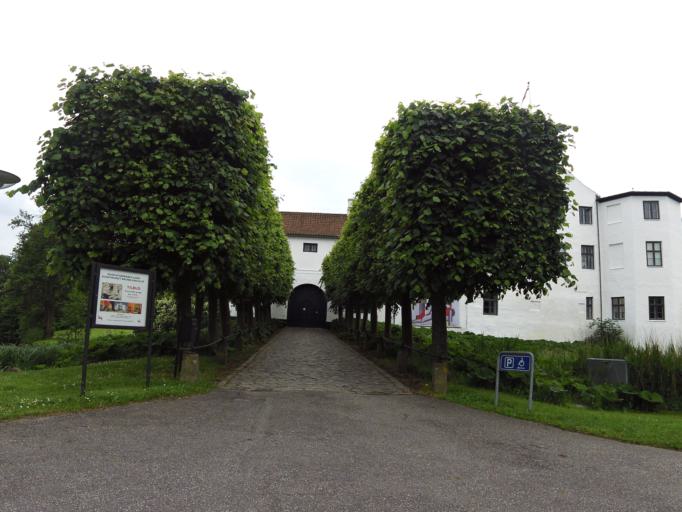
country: DK
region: South Denmark
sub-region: Aabenraa Kommune
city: Aabenraa
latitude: 55.0398
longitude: 9.4141
